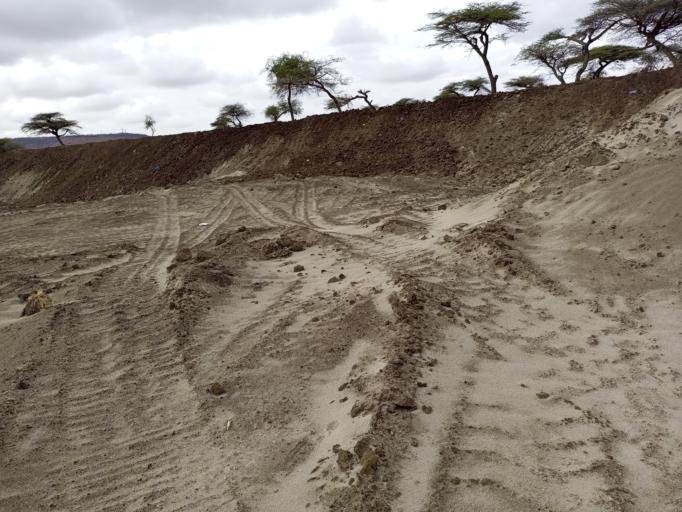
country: ET
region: Oromiya
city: Ziway
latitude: 7.9219
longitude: 38.6817
